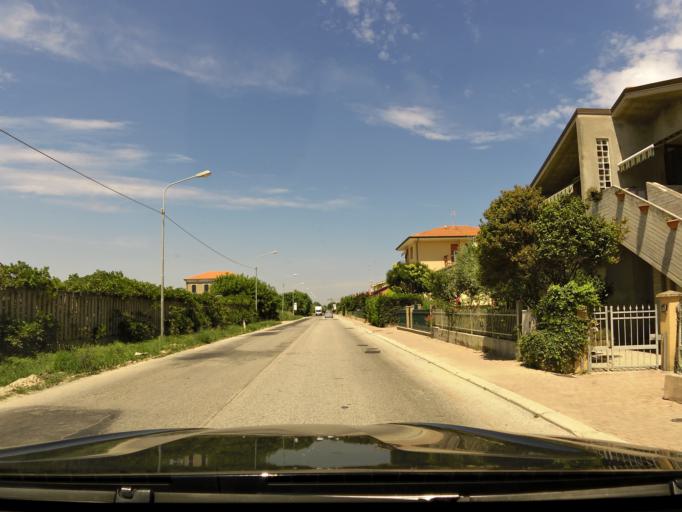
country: IT
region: The Marches
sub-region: Provincia di Ancona
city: Senigallia
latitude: 43.7401
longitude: 13.1844
